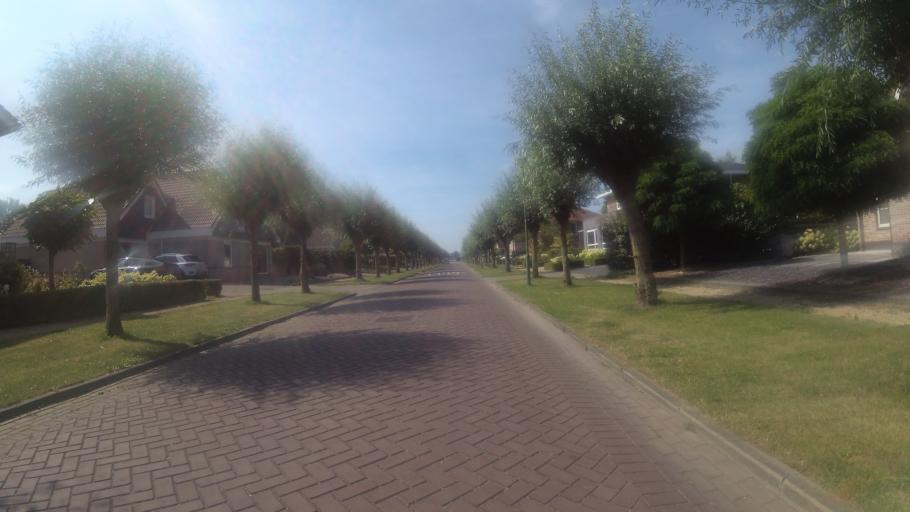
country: NL
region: Zeeland
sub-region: Gemeente Noord-Beveland
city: Kamperland
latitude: 51.5692
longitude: 3.7073
